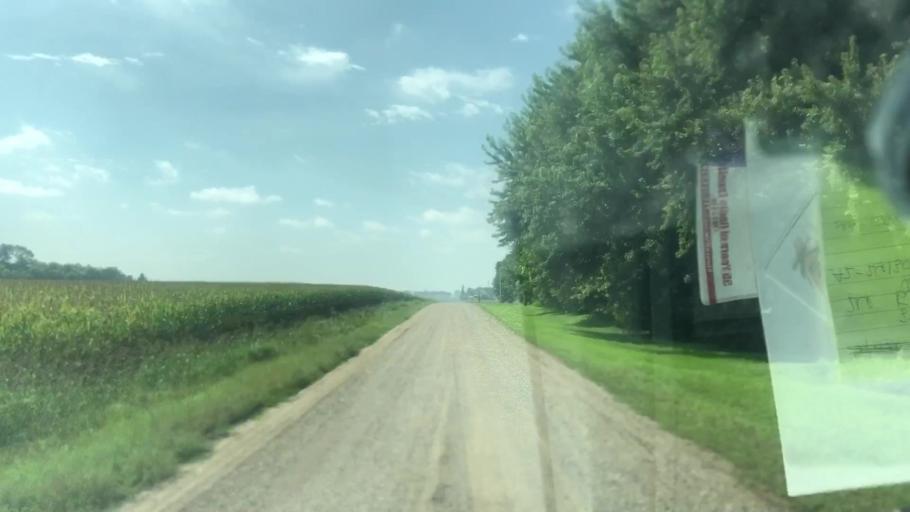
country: US
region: Iowa
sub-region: O'Brien County
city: Sheldon
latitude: 43.1922
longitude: -95.9415
